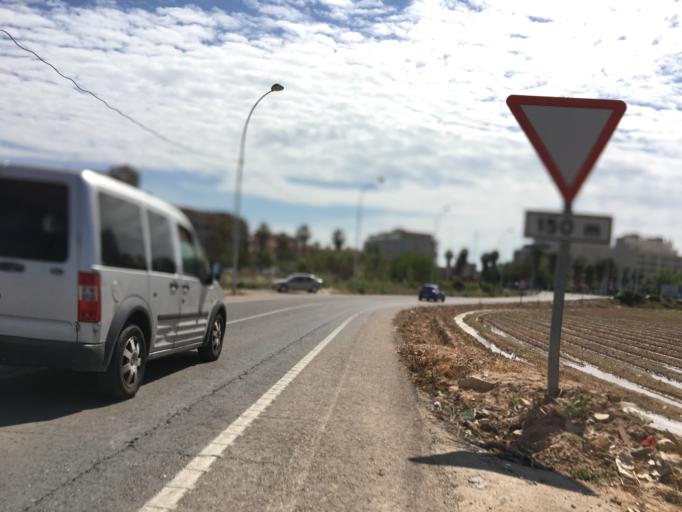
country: ES
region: Valencia
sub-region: Provincia de Valencia
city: Mislata
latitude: 39.4883
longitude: -0.4075
